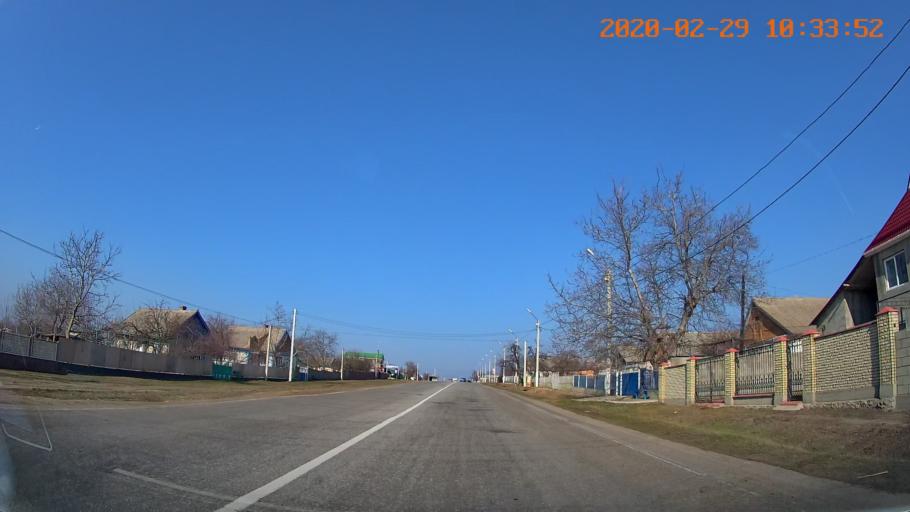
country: MD
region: Anenii Noi
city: Varnita
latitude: 46.9731
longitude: 29.5399
